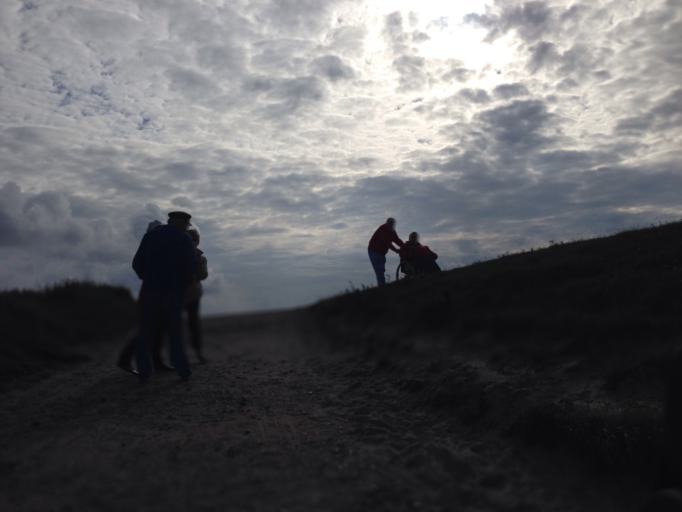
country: DE
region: Schleswig-Holstein
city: Utersum
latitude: 54.7157
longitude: 8.3969
